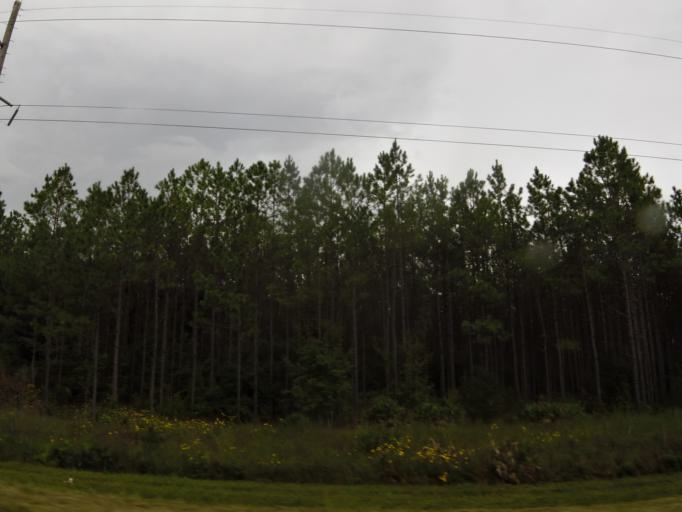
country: US
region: Florida
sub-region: Duval County
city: Baldwin
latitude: 30.4675
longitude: -82.0577
